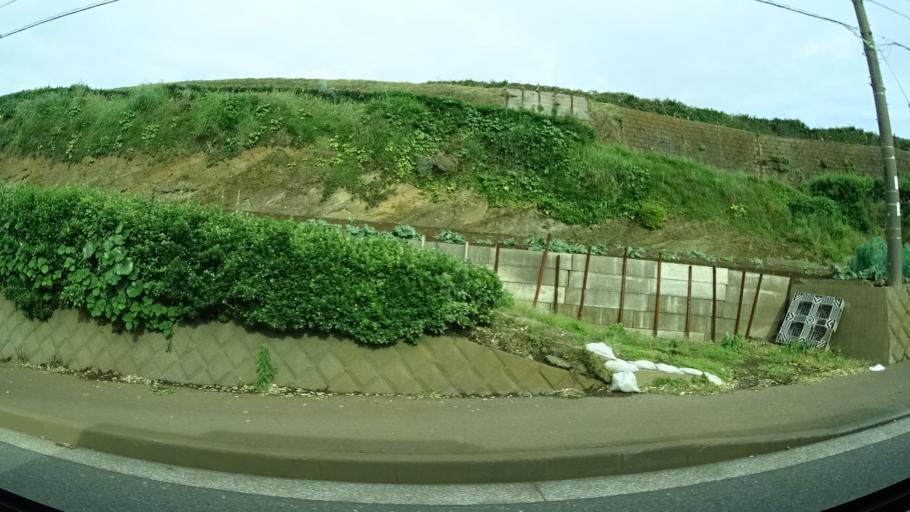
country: JP
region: Kanagawa
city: Miura
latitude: 35.1559
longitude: 139.6709
